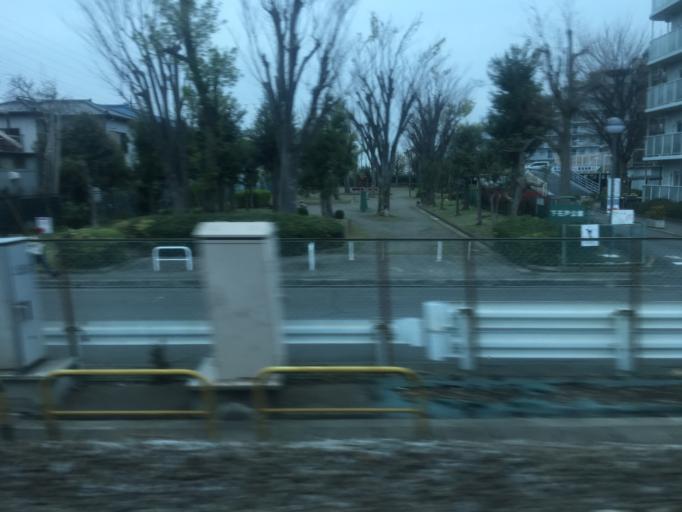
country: JP
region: Saitama
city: Okegawa
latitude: 36.0142
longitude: 139.5479
